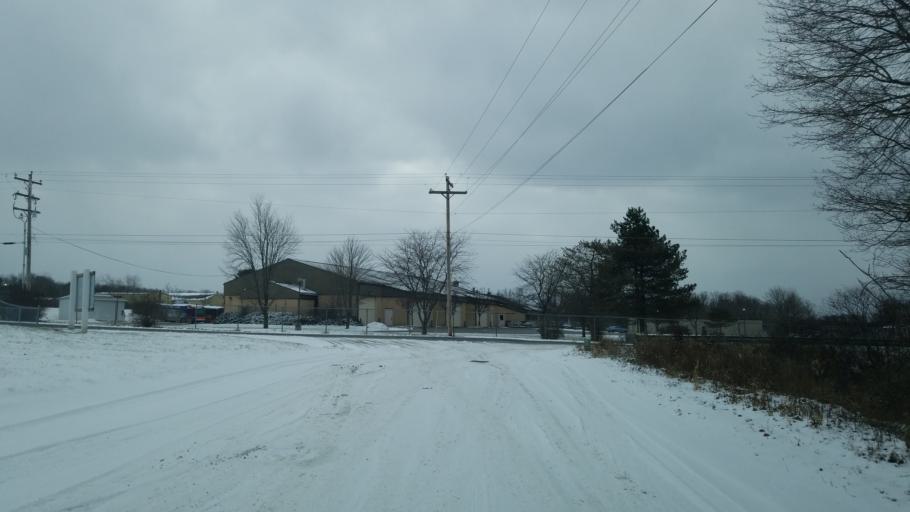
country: US
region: Pennsylvania
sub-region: Clearfield County
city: DuBois
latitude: 41.1103
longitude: -78.7313
